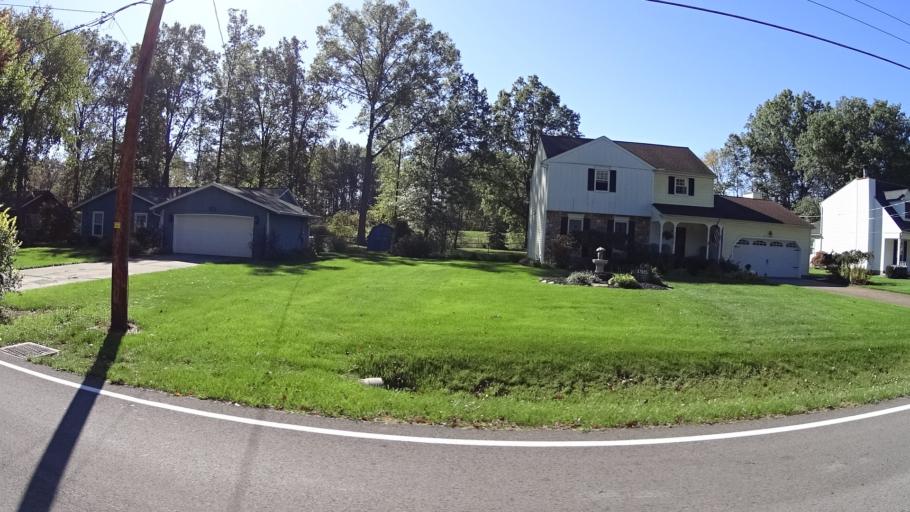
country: US
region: Ohio
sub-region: Lorain County
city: Amherst
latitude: 41.4118
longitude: -82.2469
